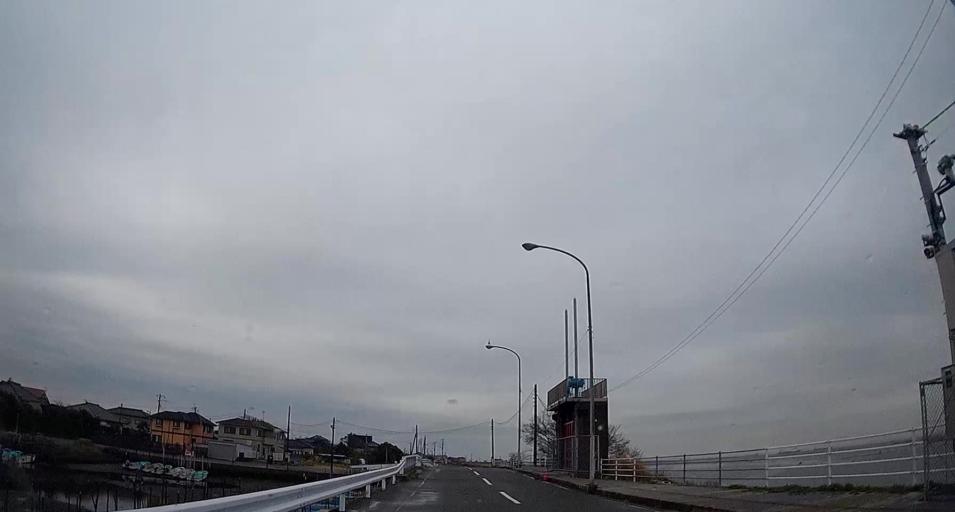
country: JP
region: Chiba
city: Kisarazu
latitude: 35.4352
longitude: 139.9123
